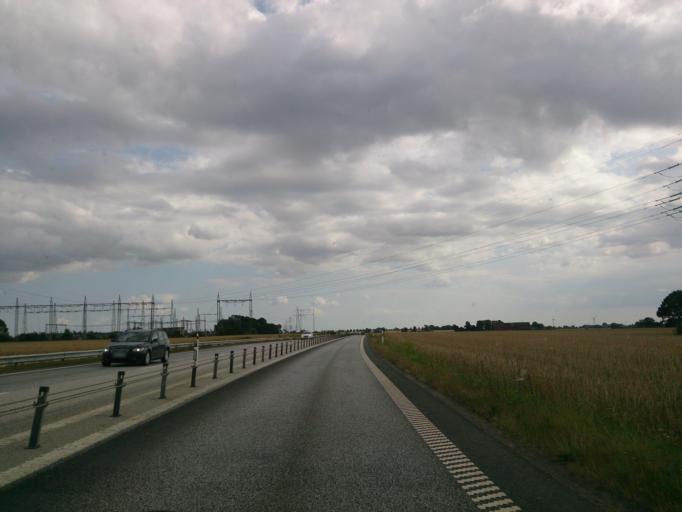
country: SE
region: Skane
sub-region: Kavlinge Kommun
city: Kaevlinge
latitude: 55.7433
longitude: 13.1433
